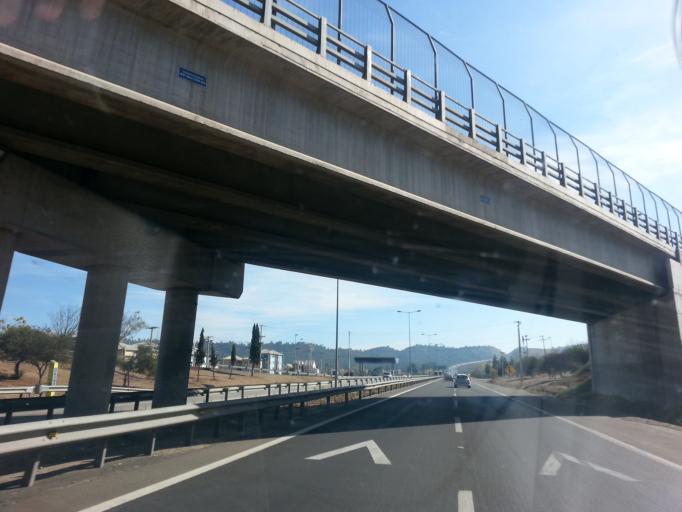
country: CL
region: Valparaiso
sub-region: Provincia de Marga Marga
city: Quilpue
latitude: -33.3072
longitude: -71.4093
